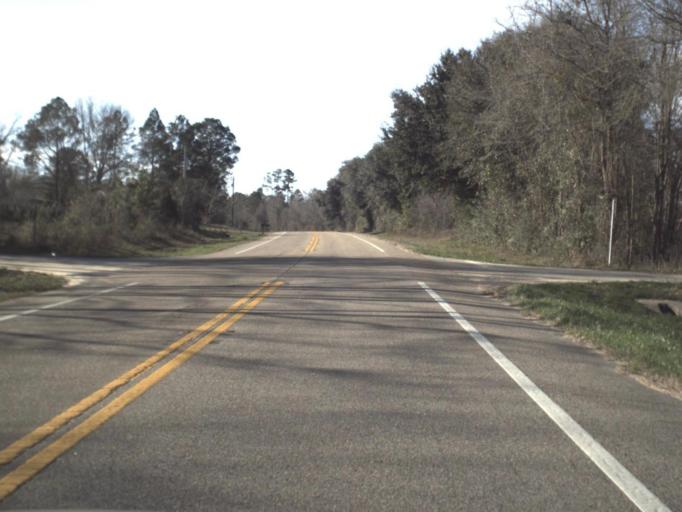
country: US
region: Florida
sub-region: Jackson County
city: Marianna
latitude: 30.6592
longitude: -85.2191
